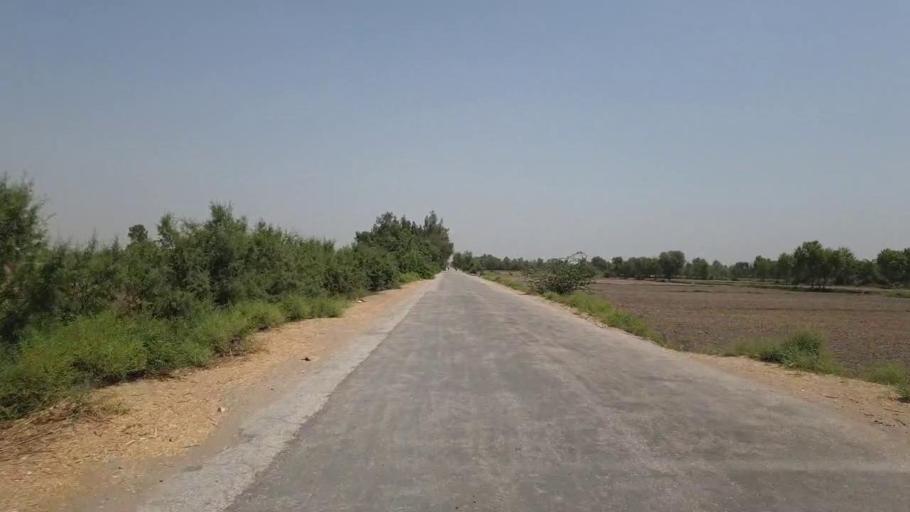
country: PK
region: Sindh
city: Adilpur
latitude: 27.9079
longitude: 69.2981
